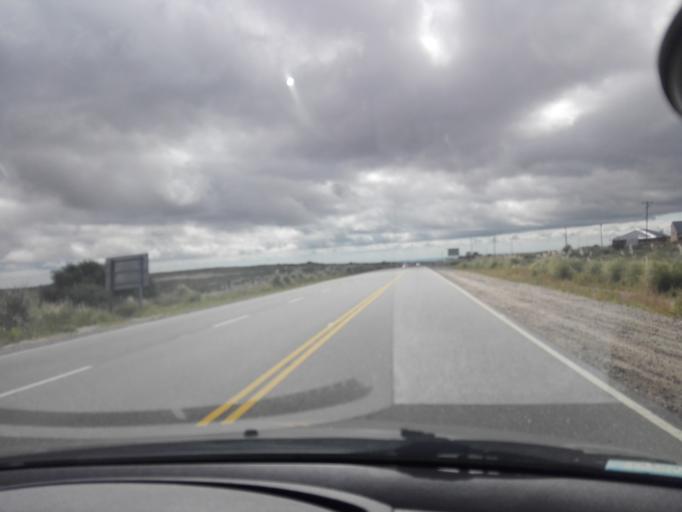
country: AR
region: Cordoba
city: Mina Clavero
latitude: -31.6174
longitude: -64.8736
